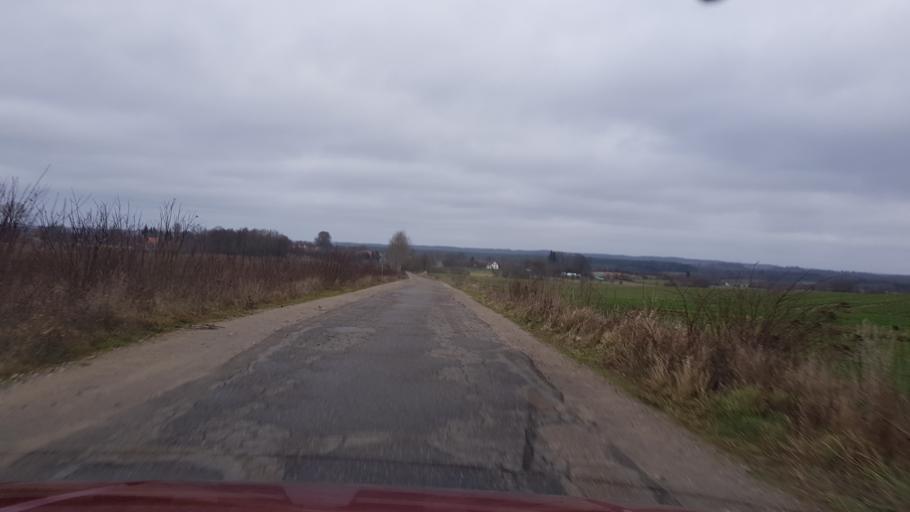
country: PL
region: Pomeranian Voivodeship
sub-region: Powiat bytowski
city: Tuchomie
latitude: 54.1577
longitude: 17.3375
